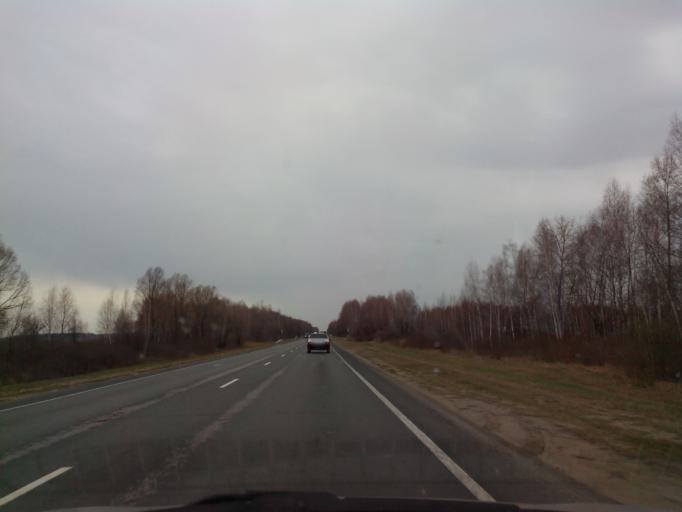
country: RU
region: Tambov
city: Michurinsk
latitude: 53.0587
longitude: 40.4540
